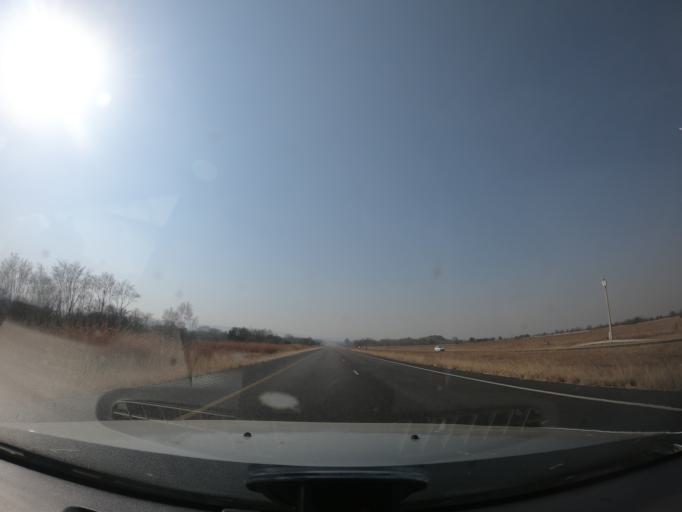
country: ZA
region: Gauteng
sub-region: City of Tshwane Metropolitan Municipality
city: Cullinan
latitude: -25.7661
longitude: 28.3939
